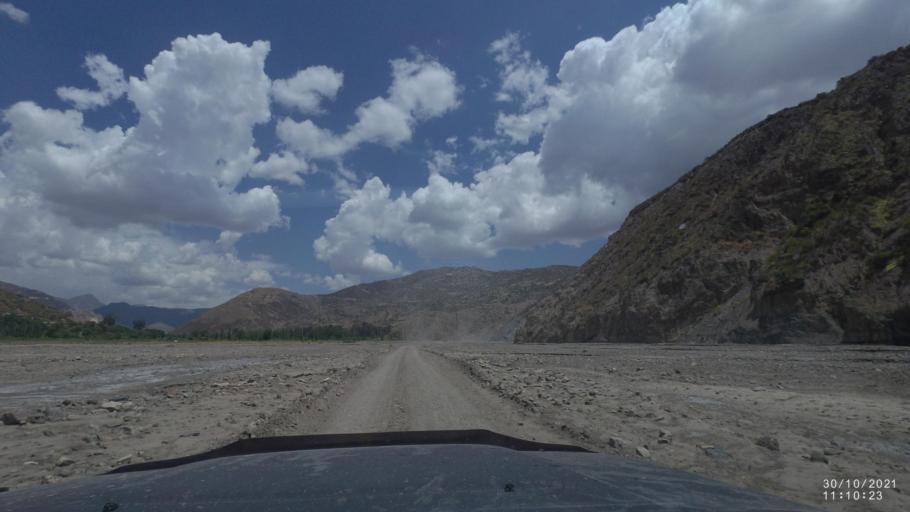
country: BO
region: Cochabamba
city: Sipe Sipe
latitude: -17.5277
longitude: -66.5595
